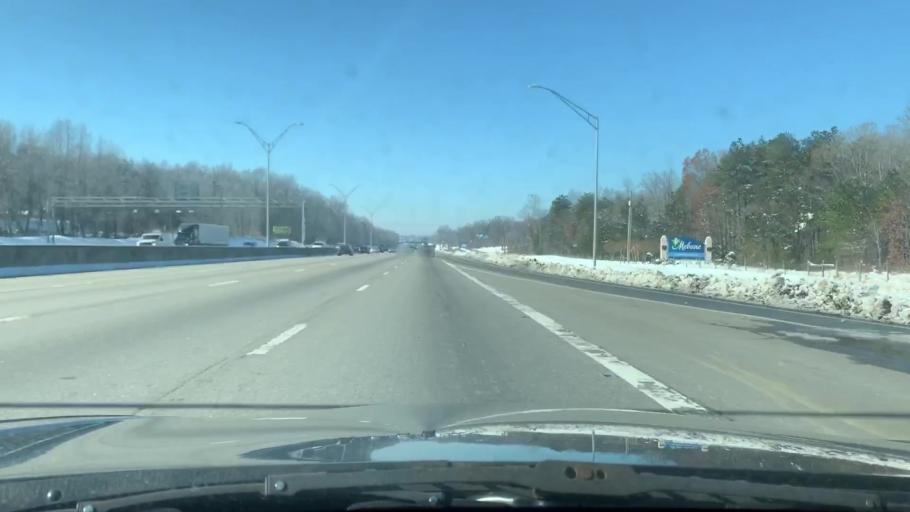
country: US
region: North Carolina
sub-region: Alamance County
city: Mebane
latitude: 36.0792
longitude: -79.2281
